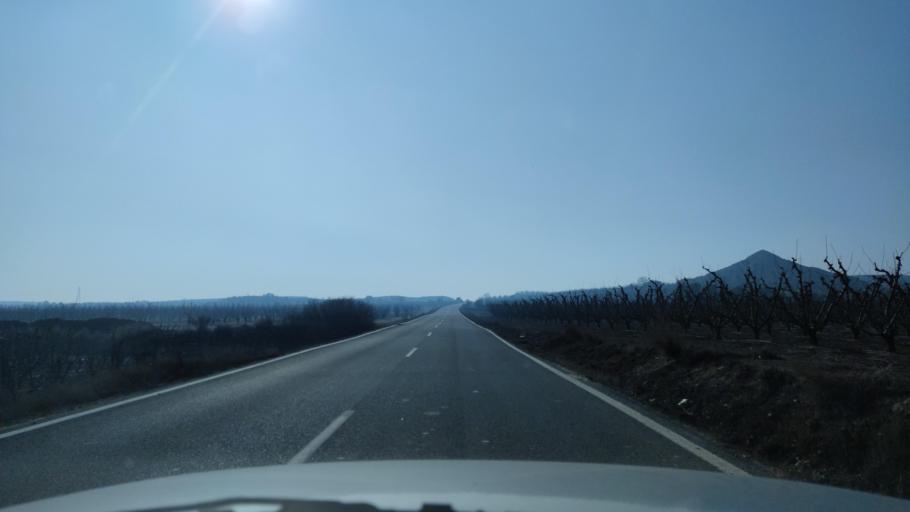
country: ES
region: Catalonia
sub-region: Provincia de Lleida
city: Seros
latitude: 41.4746
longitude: 0.3836
